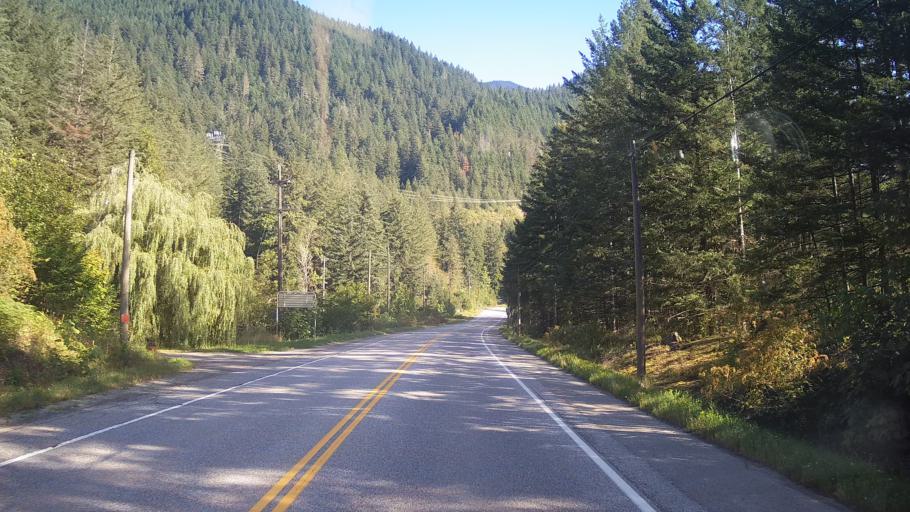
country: CA
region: British Columbia
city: Hope
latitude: 49.5531
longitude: -121.4443
